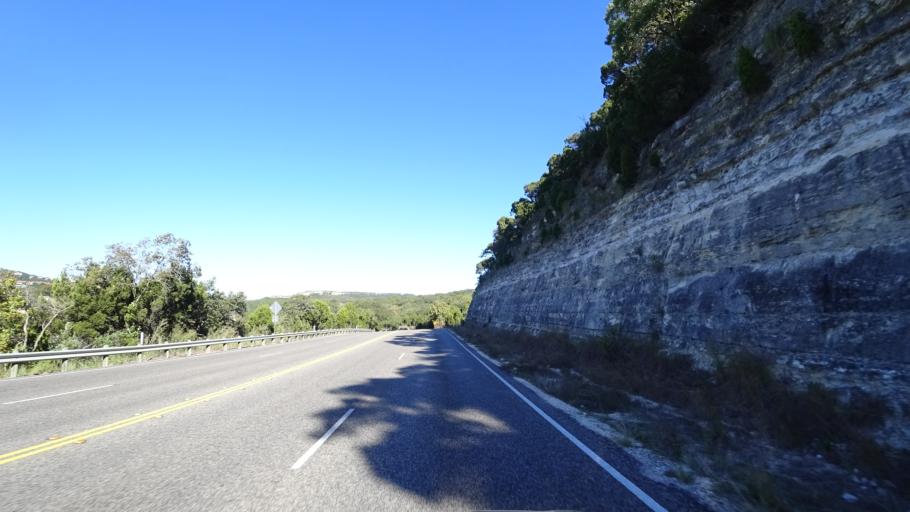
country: US
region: Texas
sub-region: Travis County
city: West Lake Hills
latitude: 30.3549
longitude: -97.7825
